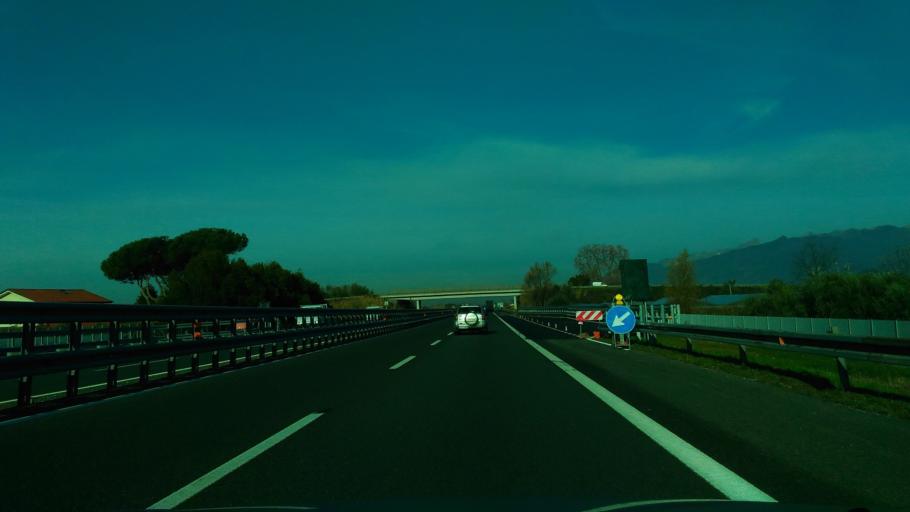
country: IT
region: Tuscany
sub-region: Provincia di Lucca
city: Camaiore
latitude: 43.9133
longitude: 10.2376
